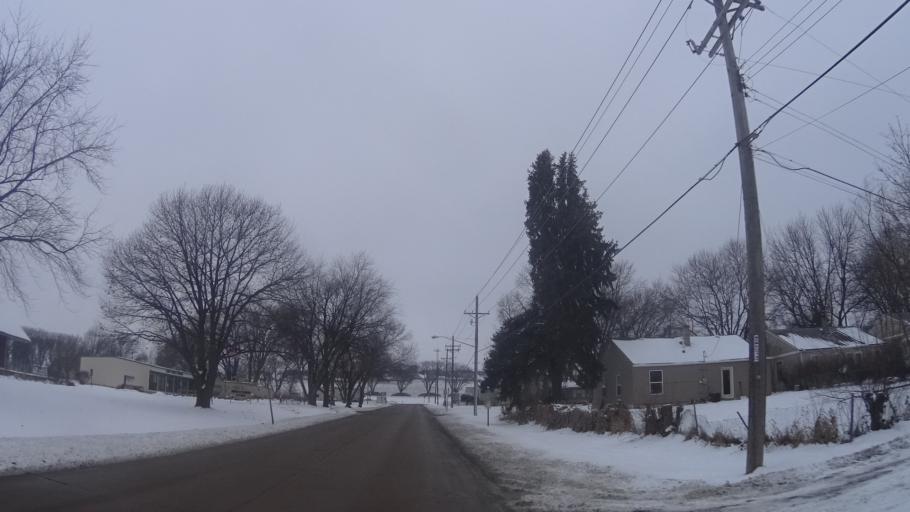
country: US
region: Nebraska
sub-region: Sarpy County
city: Bellevue
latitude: 41.1345
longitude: -95.9047
